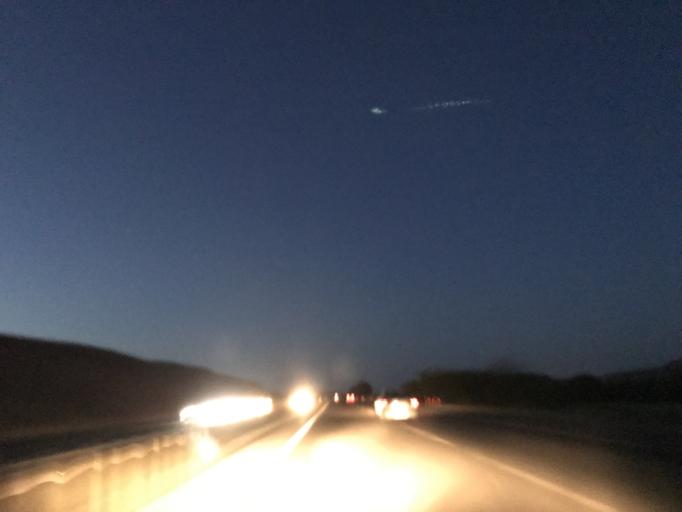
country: TR
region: Yozgat
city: Yerkoy
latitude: 39.6673
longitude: 34.5709
